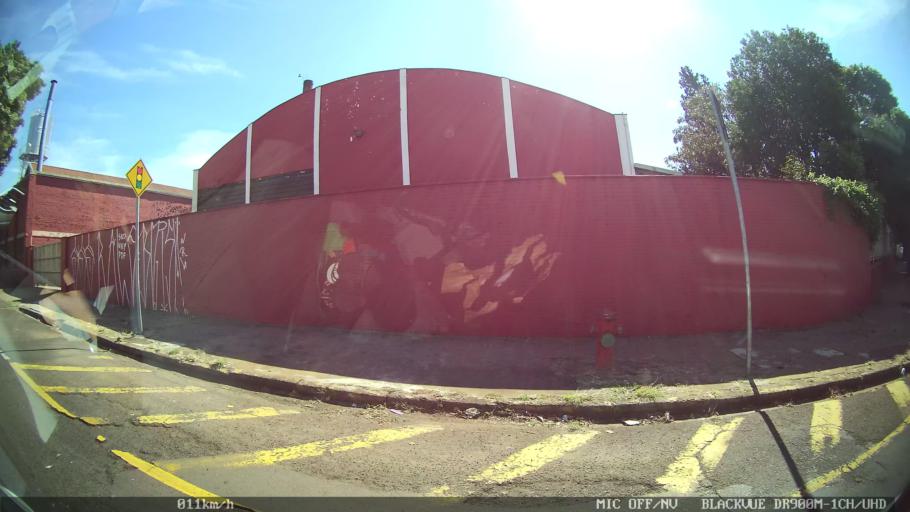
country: BR
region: Sao Paulo
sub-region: Franca
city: Franca
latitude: -20.5375
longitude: -47.4133
